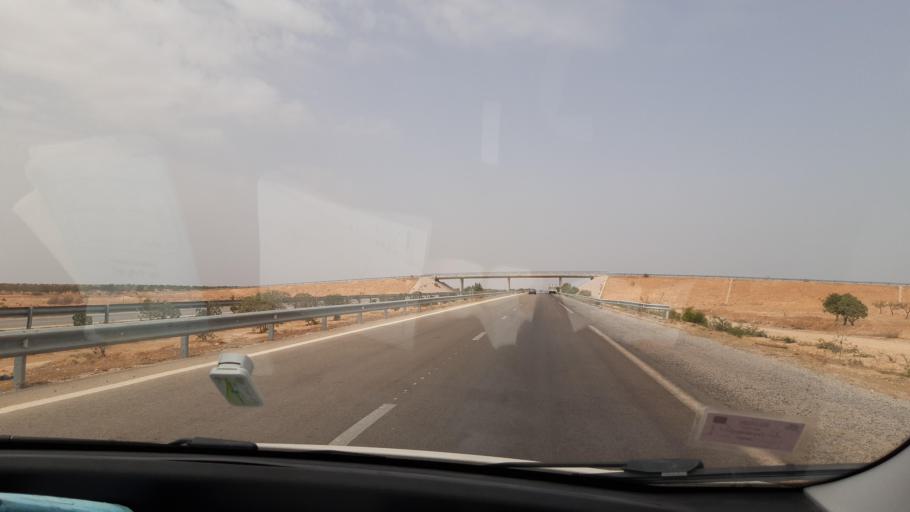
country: TN
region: Safaqis
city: Sfax
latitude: 34.8557
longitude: 10.6826
